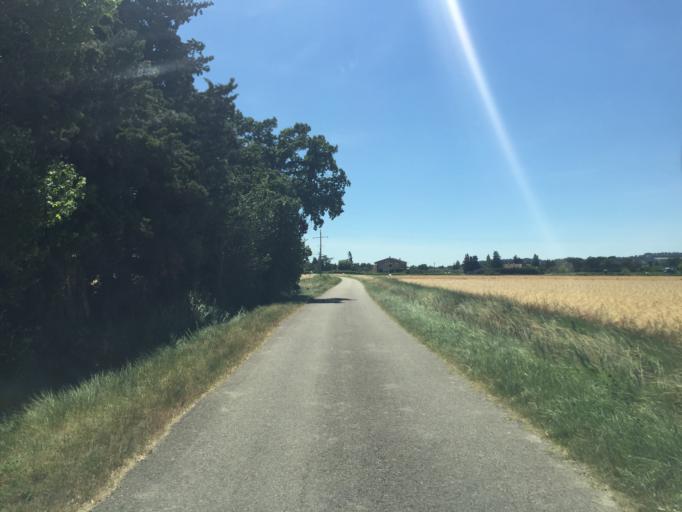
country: FR
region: Provence-Alpes-Cote d'Azur
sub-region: Departement du Vaucluse
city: Bedarrides
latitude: 44.0477
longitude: 4.9132
